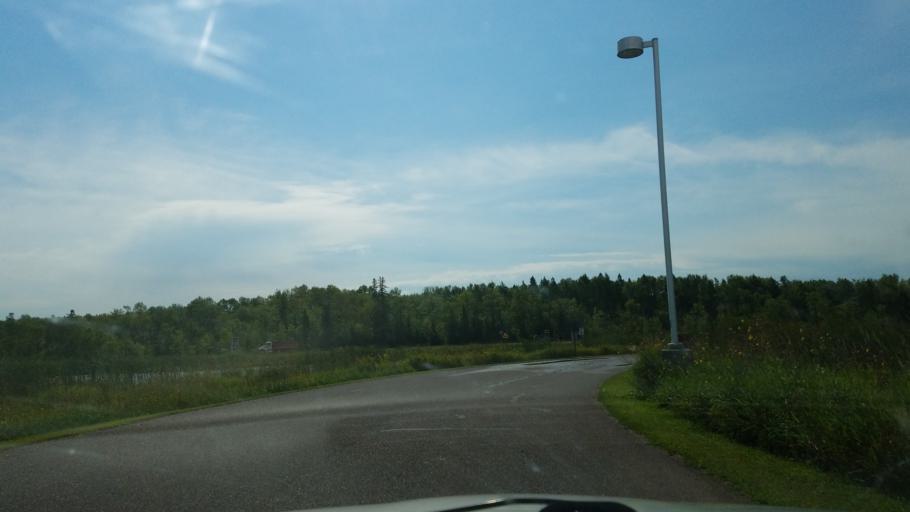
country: US
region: Wisconsin
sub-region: Ashland County
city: Ashland
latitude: 46.5829
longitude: -90.9635
